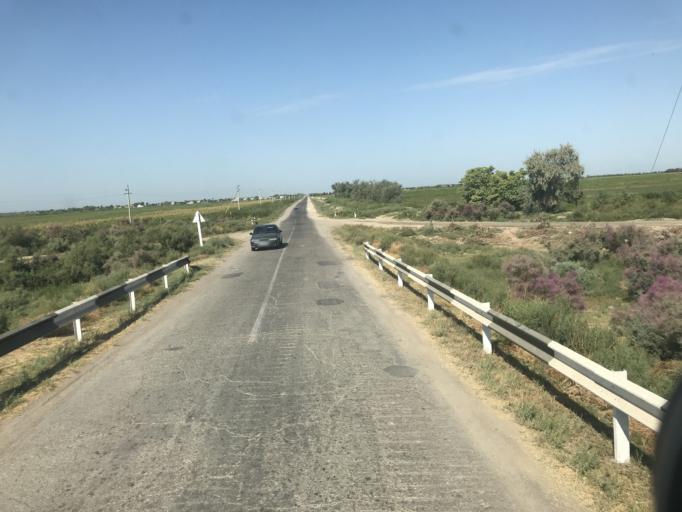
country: KZ
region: Ongtustik Qazaqstan
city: Myrzakent
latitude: 40.6843
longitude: 68.6334
